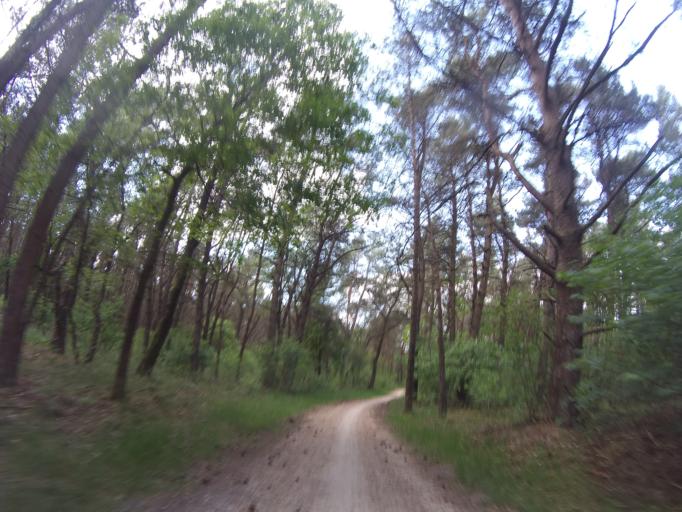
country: NL
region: Gelderland
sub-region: Gemeente Barneveld
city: Stroe
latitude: 52.1713
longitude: 5.7149
